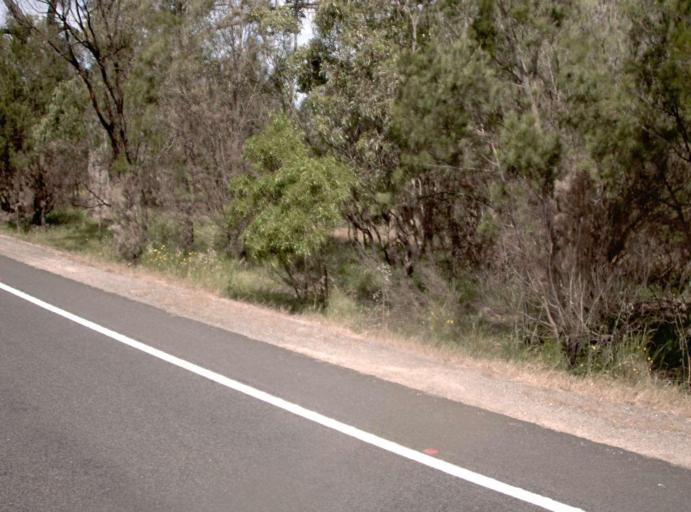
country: AU
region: Victoria
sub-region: East Gippsland
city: Bairnsdale
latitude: -37.8648
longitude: 147.4963
